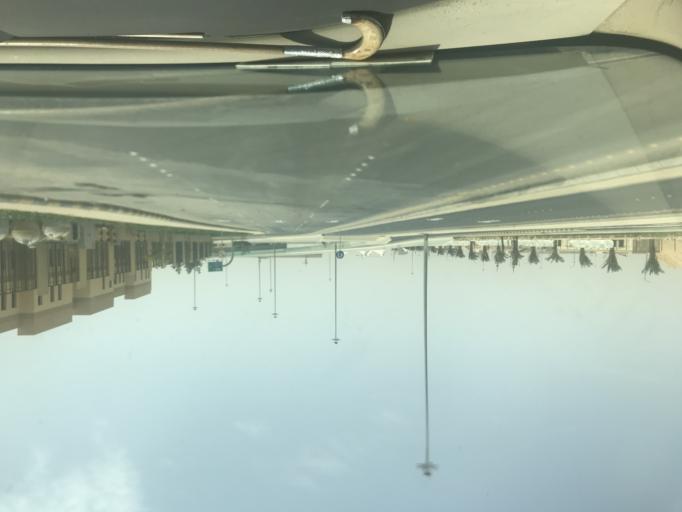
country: SA
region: Ar Riyad
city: Riyadh
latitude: 24.8226
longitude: 46.6987
